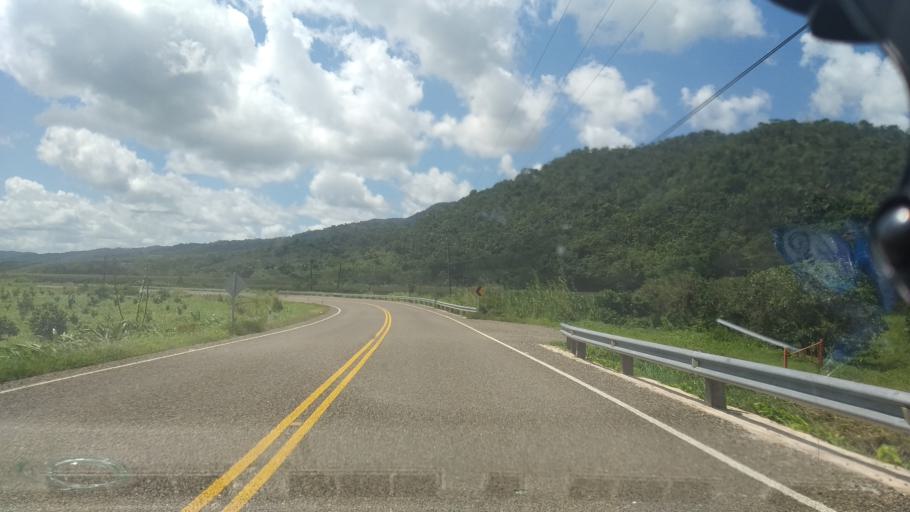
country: BZ
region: Stann Creek
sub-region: Dangriga
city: Dangriga
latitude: 17.0199
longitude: -88.4898
